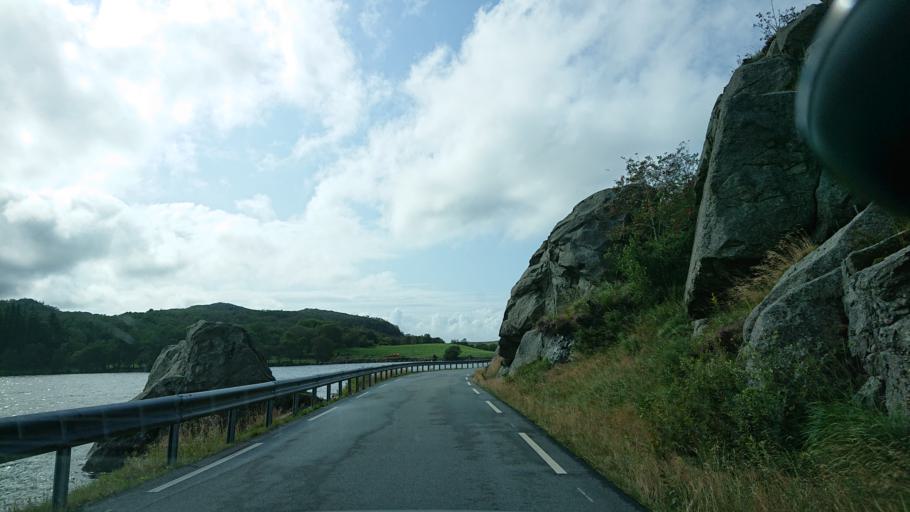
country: NO
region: Rogaland
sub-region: Gjesdal
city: Algard
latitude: 58.6763
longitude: 5.8281
